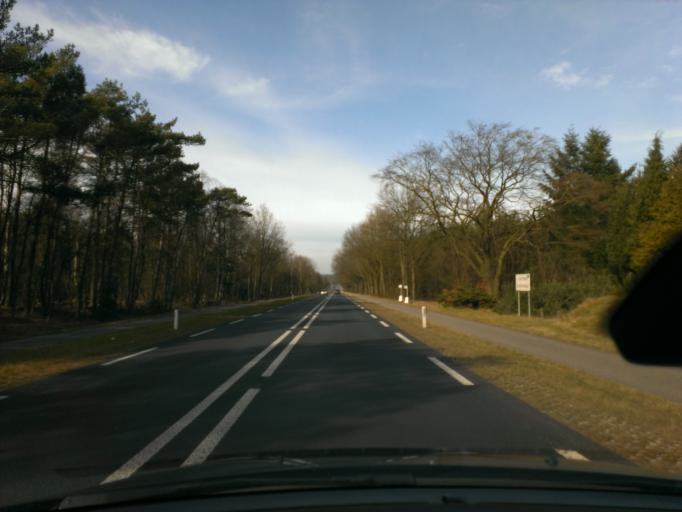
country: NL
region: Gelderland
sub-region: Gemeente Oldebroek
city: Oldebroek
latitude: 52.3886
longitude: 5.9079
